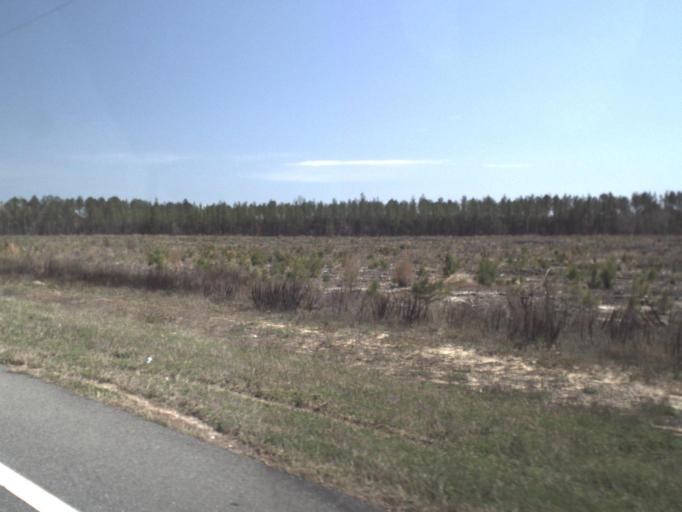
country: US
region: Florida
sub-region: Gadsden County
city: Quincy
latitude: 30.4160
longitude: -84.6577
